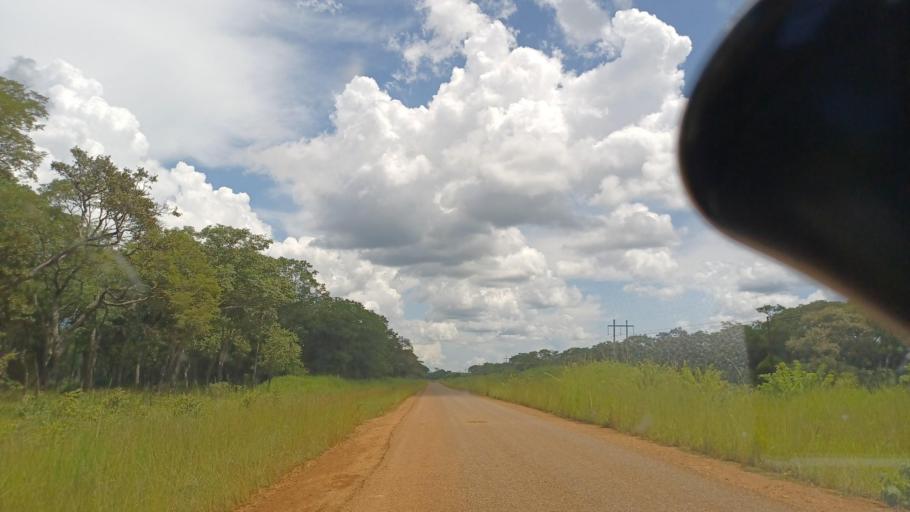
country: ZM
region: North-Western
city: Solwezi
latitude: -12.7110
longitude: 26.0261
